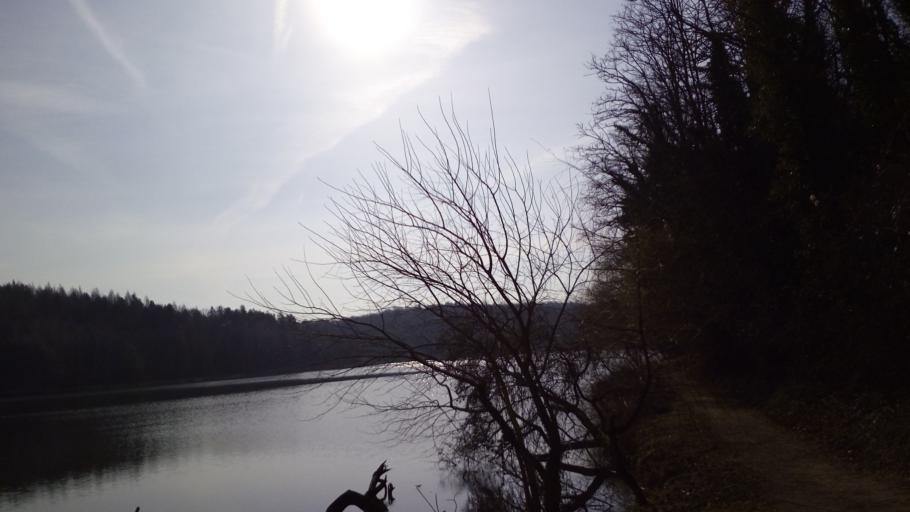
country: HU
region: Baranya
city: Pellerd
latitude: 46.0083
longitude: 18.1999
